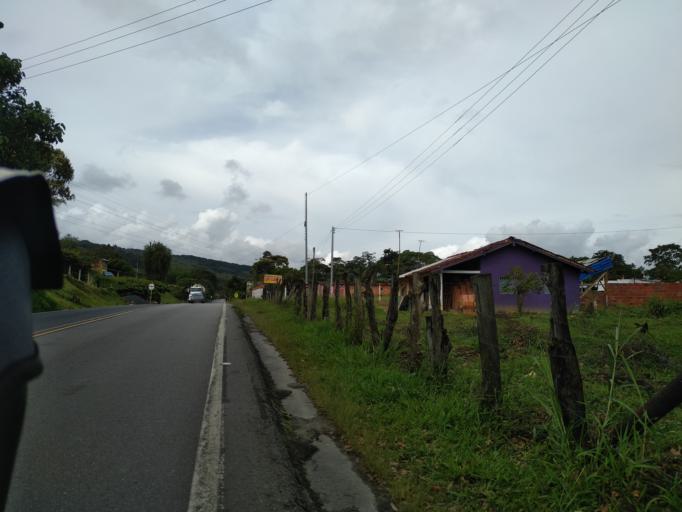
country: CO
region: Santander
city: Suaita
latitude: 6.0905
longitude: -73.3854
